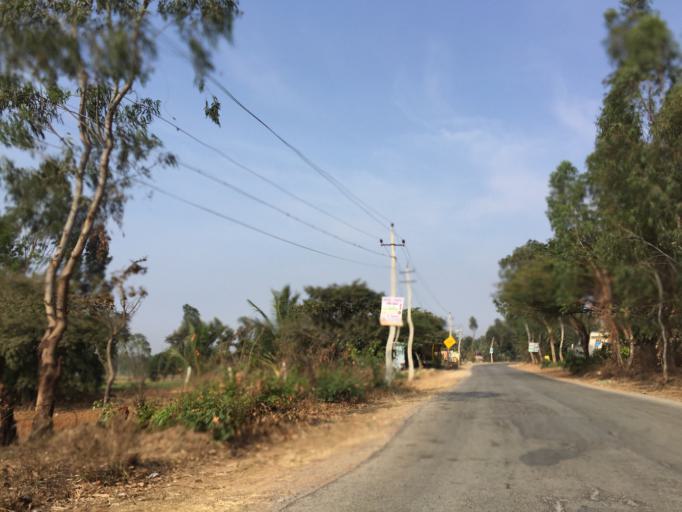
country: IN
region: Karnataka
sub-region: Chikkaballapur
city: Chik Ballapur
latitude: 13.3499
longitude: 77.6618
